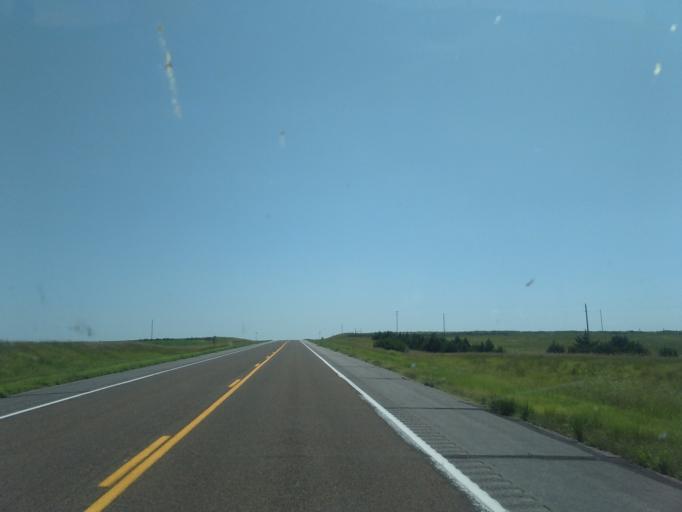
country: US
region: Nebraska
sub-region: Hitchcock County
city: Trenton
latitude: 40.1762
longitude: -101.1195
